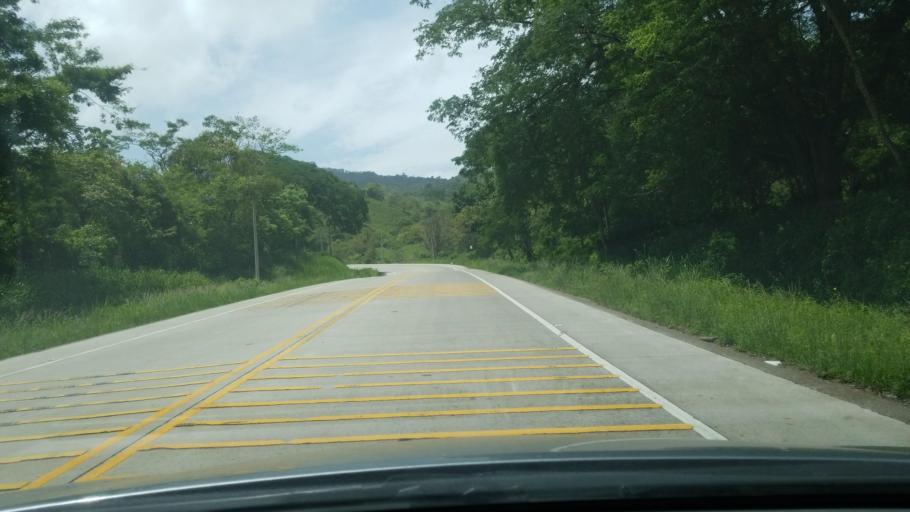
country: HN
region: Copan
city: Agua Caliente
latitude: 14.8770
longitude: -88.7795
